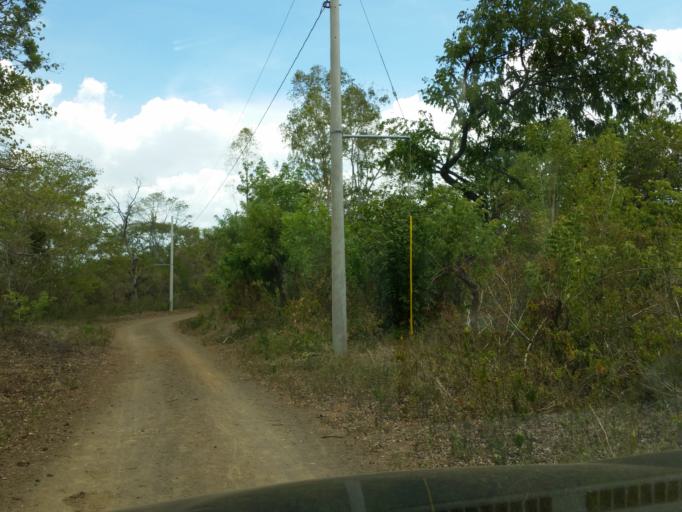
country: NI
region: Managua
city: Carlos Fonseca Amador
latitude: 11.9601
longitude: -86.4346
